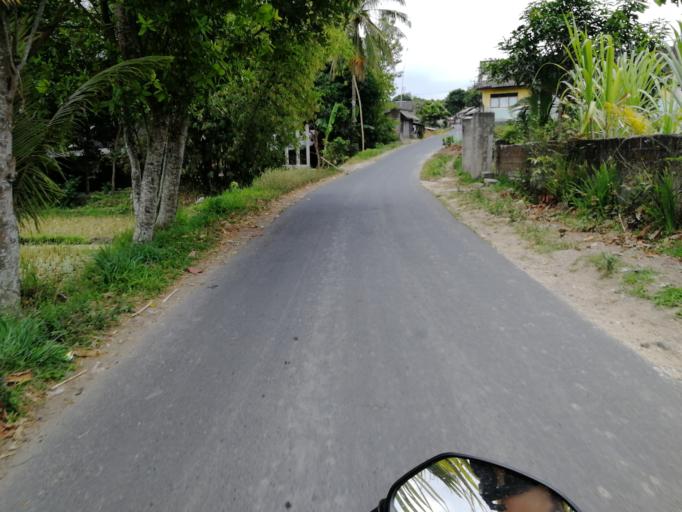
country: ID
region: West Nusa Tenggara
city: Pediti
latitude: -8.5702
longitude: 116.3294
